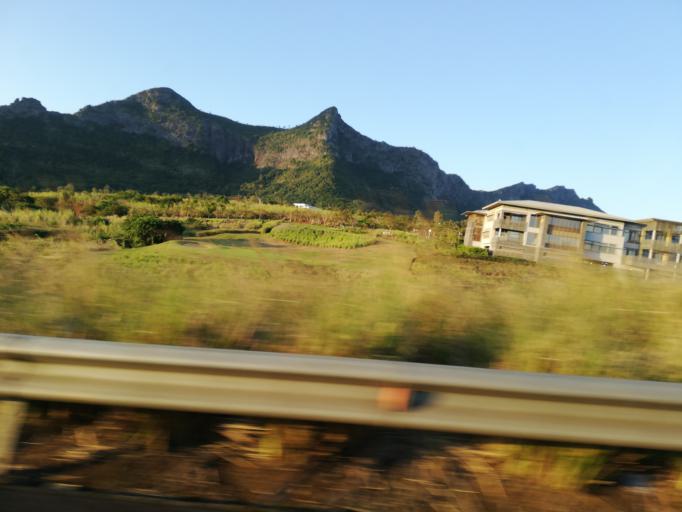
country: MU
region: Moka
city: Moka
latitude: -20.2234
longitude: 57.4913
